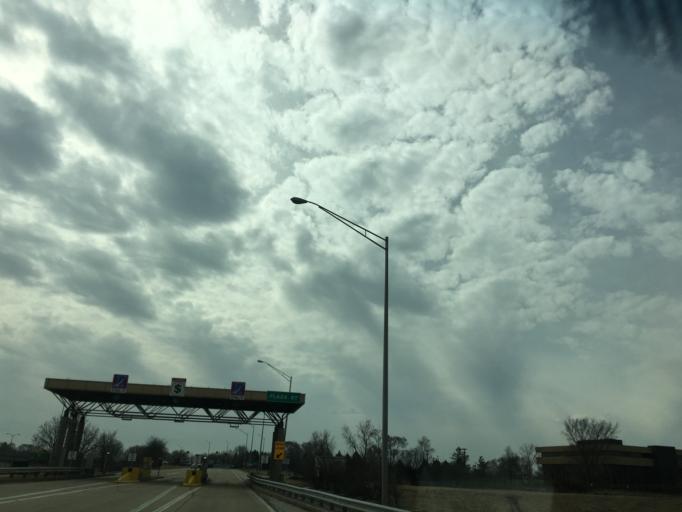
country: US
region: Illinois
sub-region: DuPage County
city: Woodridge
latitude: 41.7533
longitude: -88.0360
